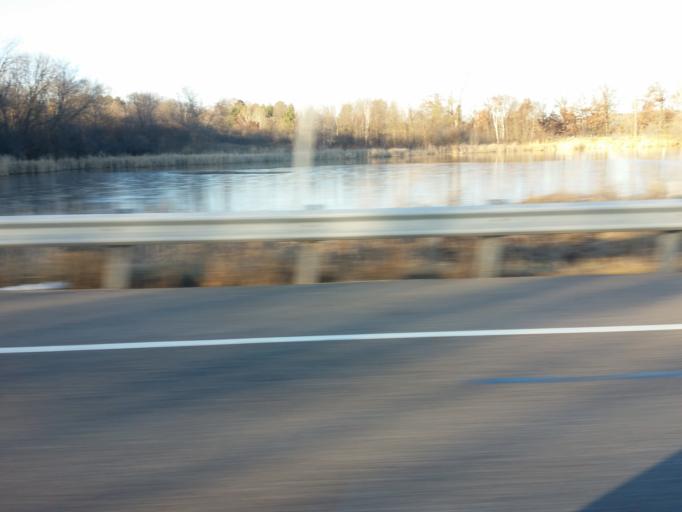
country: US
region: Minnesota
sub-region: Washington County
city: Stillwater
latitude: 45.0800
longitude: -92.8494
